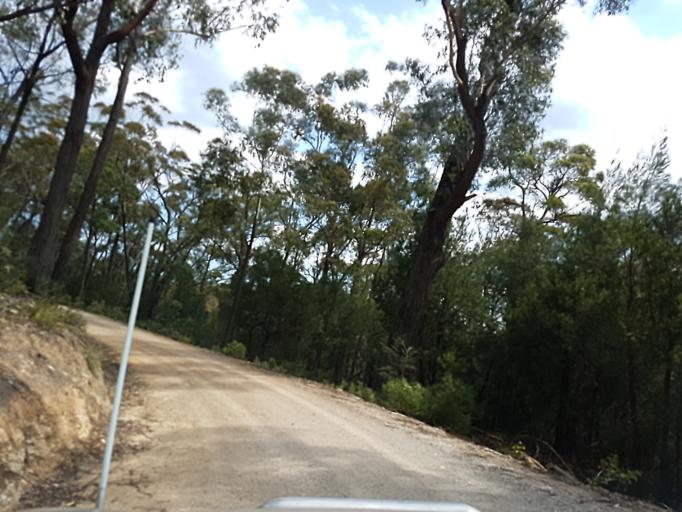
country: AU
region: Victoria
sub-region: East Gippsland
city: Lakes Entrance
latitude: -37.4054
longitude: 148.2328
